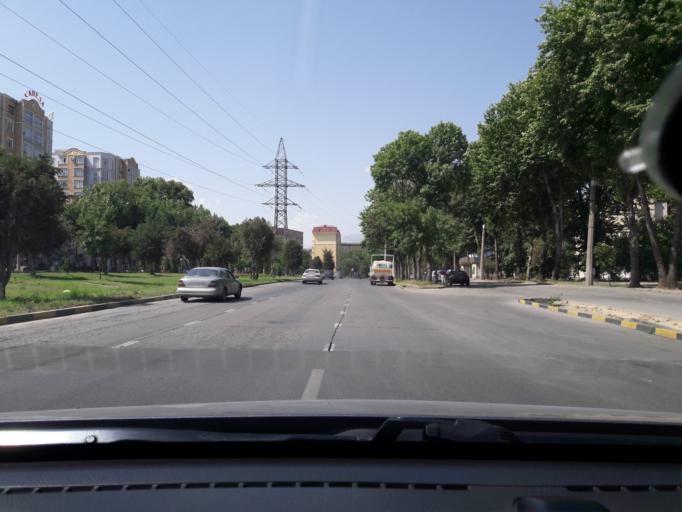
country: TJ
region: Dushanbe
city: Dushanbe
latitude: 38.5871
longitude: 68.7413
